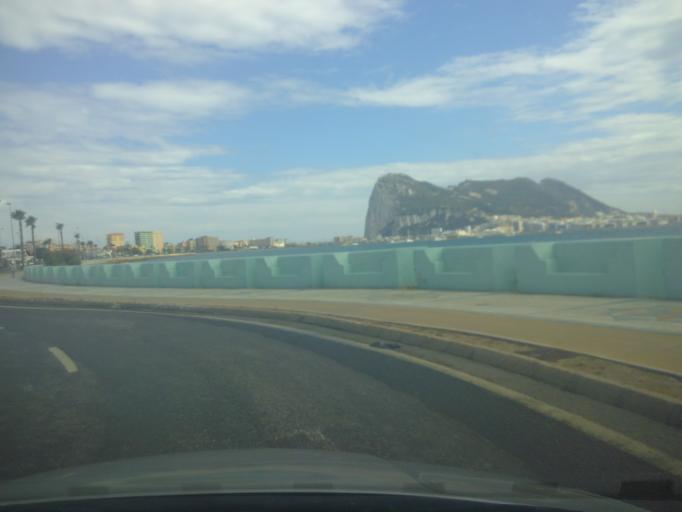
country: ES
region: Andalusia
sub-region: Provincia de Cadiz
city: La Linea de la Concepcion
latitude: 36.1682
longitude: -5.3687
